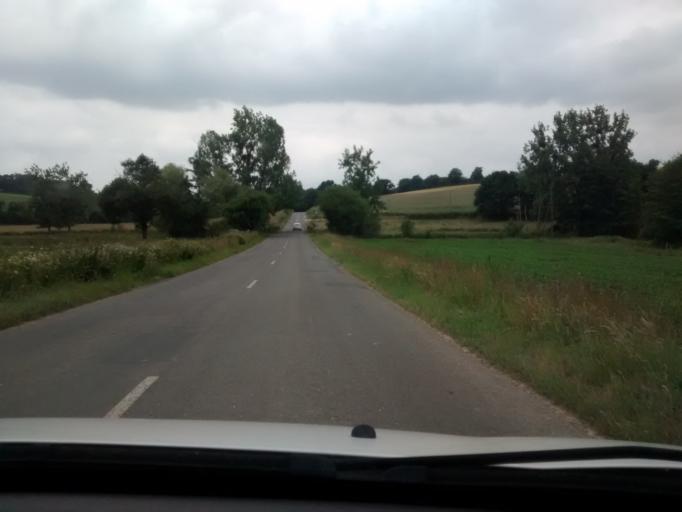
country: FR
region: Brittany
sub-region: Departement d'Ille-et-Vilaine
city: La Bouexiere
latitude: 48.1954
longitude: -1.4668
